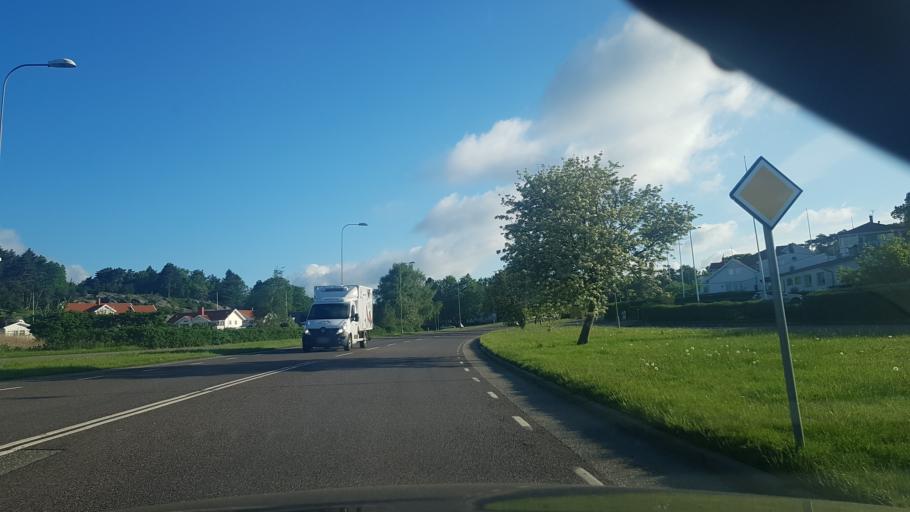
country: SE
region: Vaestra Goetaland
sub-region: Goteborg
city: Majorna
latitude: 57.6435
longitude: 11.8806
